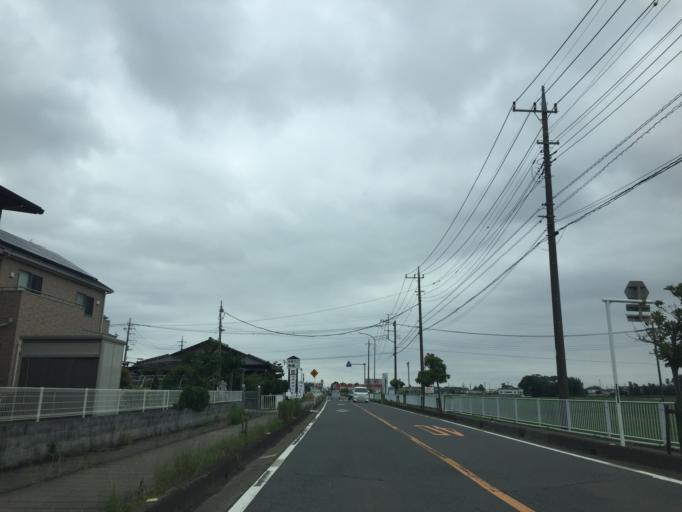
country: JP
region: Saitama
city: Kamifukuoka
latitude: 35.8873
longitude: 139.5401
